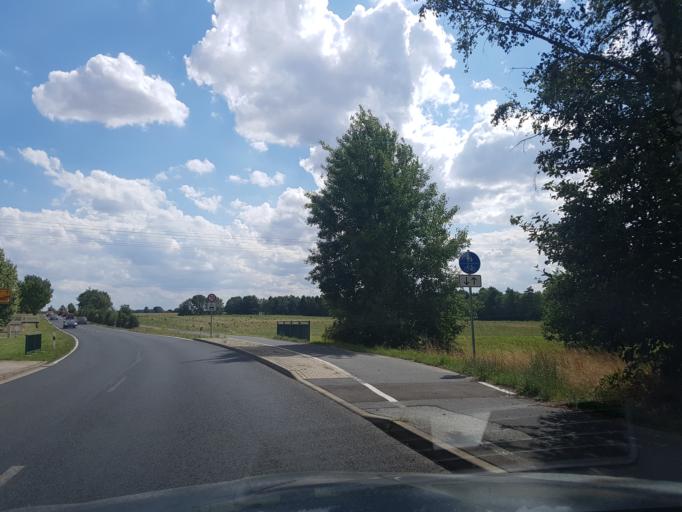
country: DE
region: Saxony
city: Grossenhain
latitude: 51.2766
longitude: 13.5323
